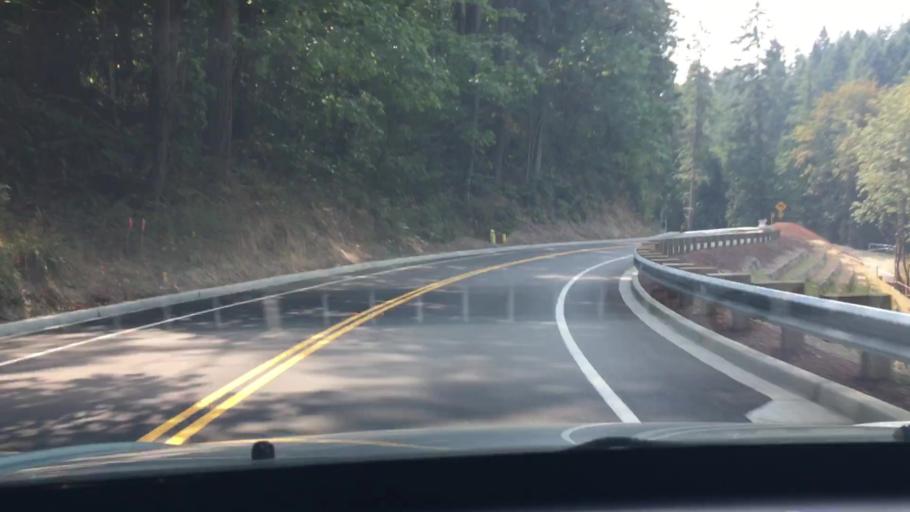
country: US
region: Washington
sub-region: King County
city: City of Sammamish
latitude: 47.5776
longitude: -122.0570
